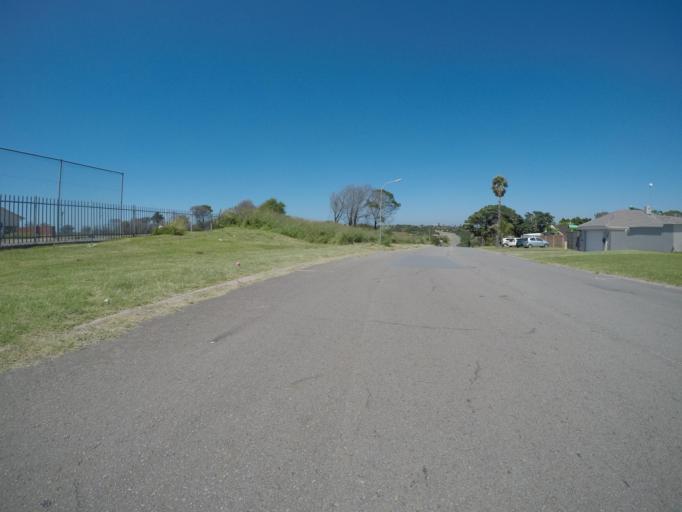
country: ZA
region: Eastern Cape
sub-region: Buffalo City Metropolitan Municipality
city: East London
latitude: -32.9718
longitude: 27.9492
